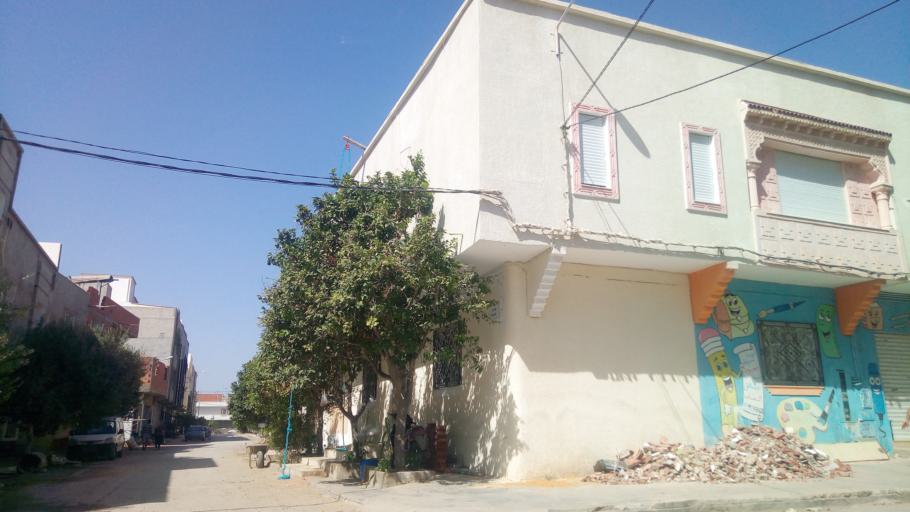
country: TN
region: Nabul
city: Dar Chabanne
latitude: 36.4670
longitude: 10.7421
